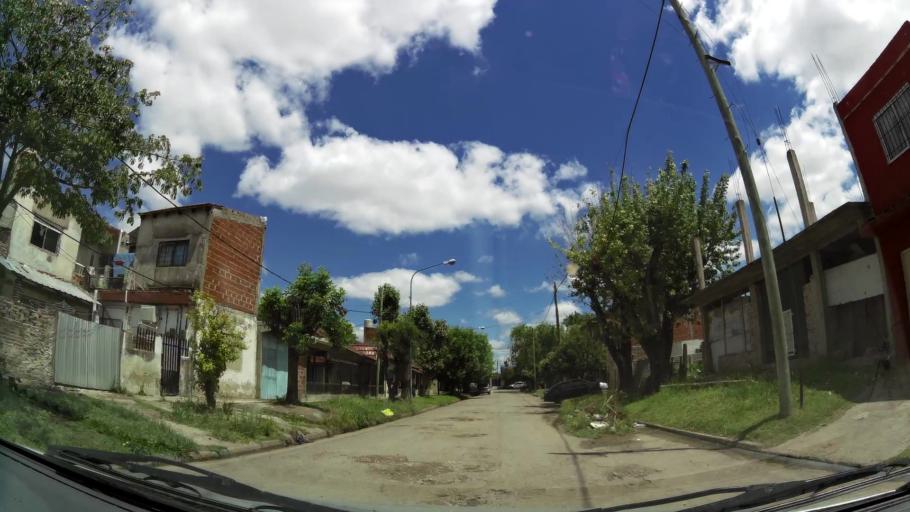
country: AR
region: Buenos Aires
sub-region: Partido de Lanus
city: Lanus
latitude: -34.7202
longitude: -58.4218
